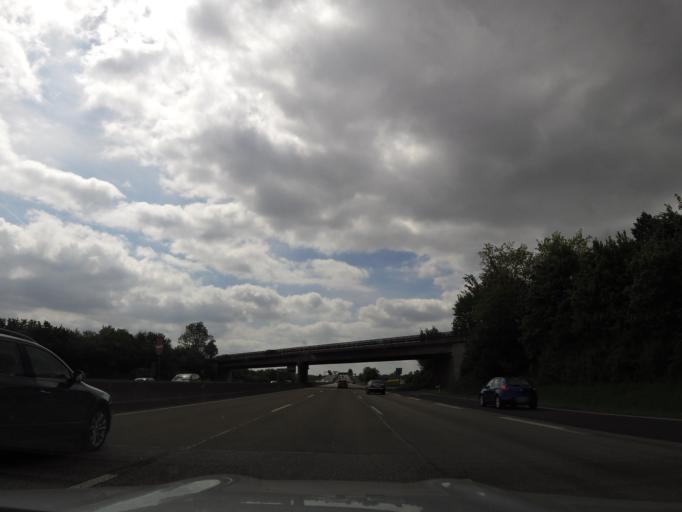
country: DE
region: Hesse
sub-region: Regierungsbezirk Darmstadt
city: Ober-Morlen
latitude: 50.4073
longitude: 8.7003
